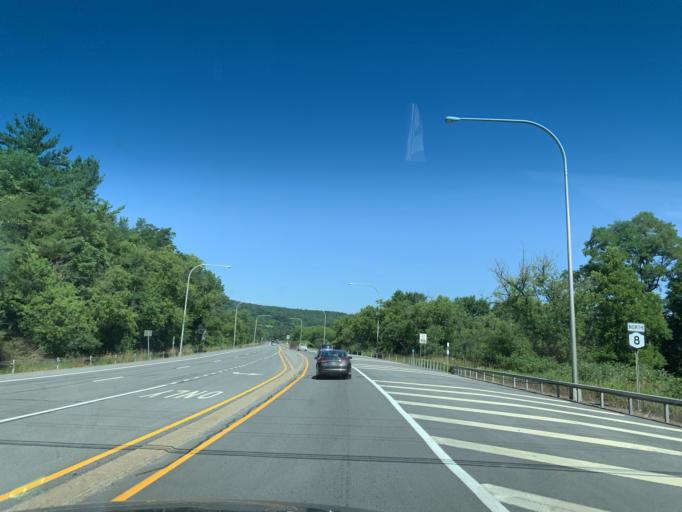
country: US
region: New York
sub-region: Delaware County
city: Sidney
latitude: 42.3094
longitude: -75.4046
